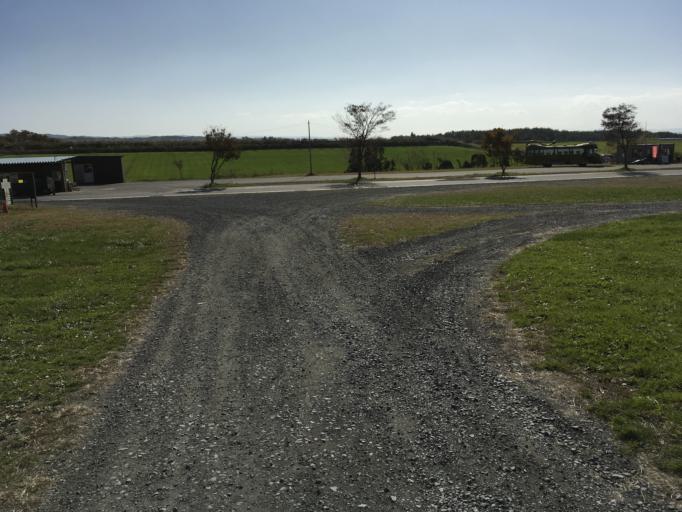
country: JP
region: Iwate
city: Ichinoseki
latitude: 38.8094
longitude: 141.2600
